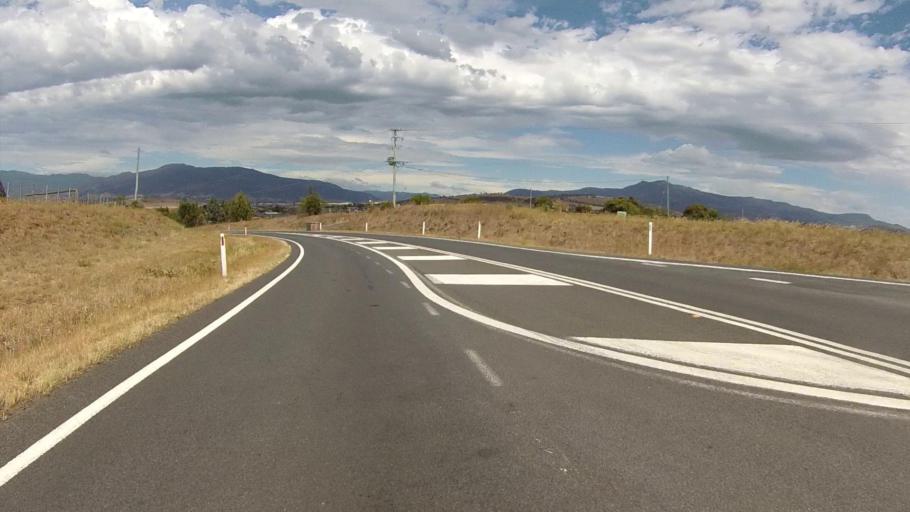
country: AU
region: Tasmania
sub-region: Brighton
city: Bridgewater
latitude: -42.6965
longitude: 147.2704
